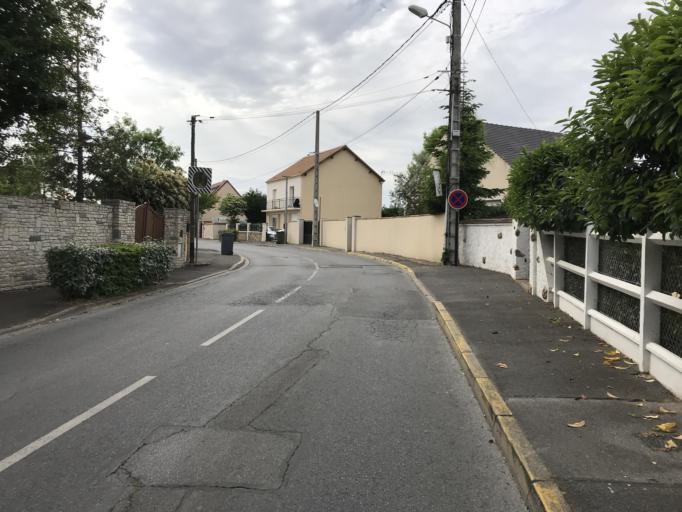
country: FR
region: Ile-de-France
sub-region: Departement de l'Essonne
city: La Ville-du-Bois
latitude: 48.6647
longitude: 2.2615
